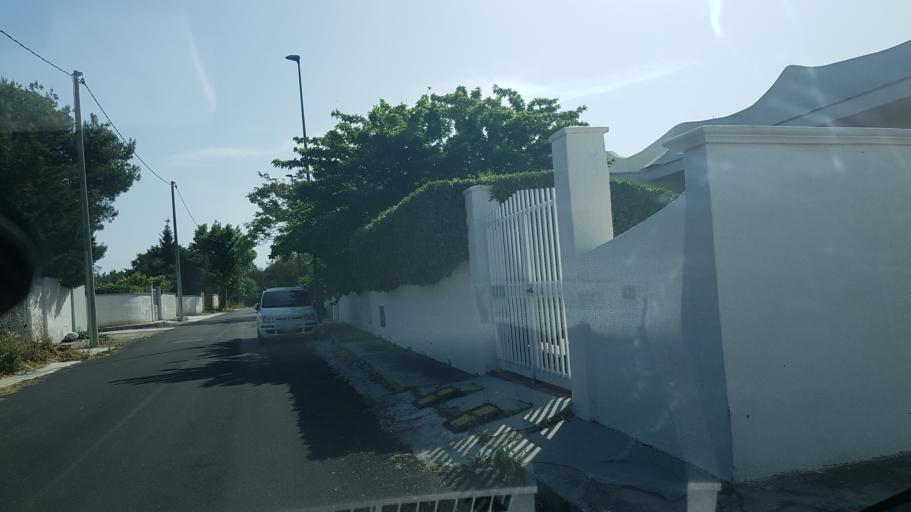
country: IT
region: Apulia
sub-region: Provincia di Brindisi
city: Torchiarolo
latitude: 40.5150
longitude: 18.0911
